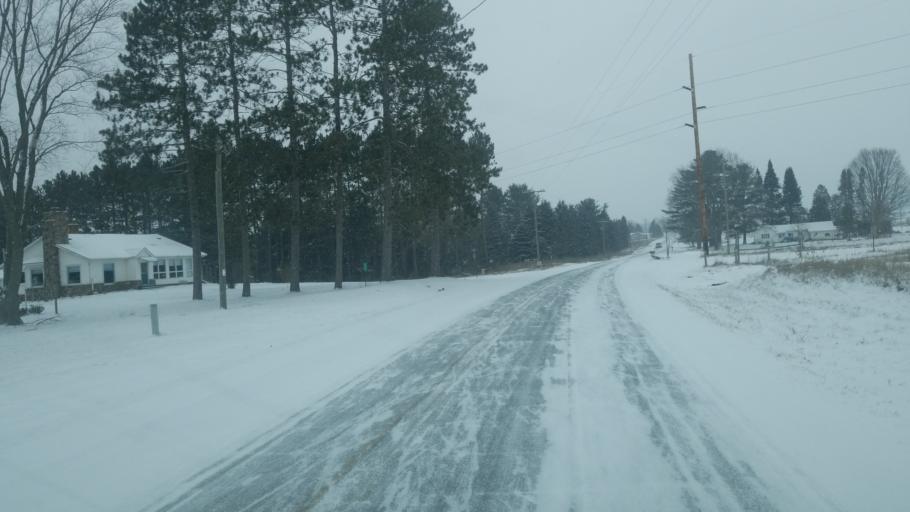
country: US
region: Michigan
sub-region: Osceola County
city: Reed City
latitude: 43.8140
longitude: -85.4040
